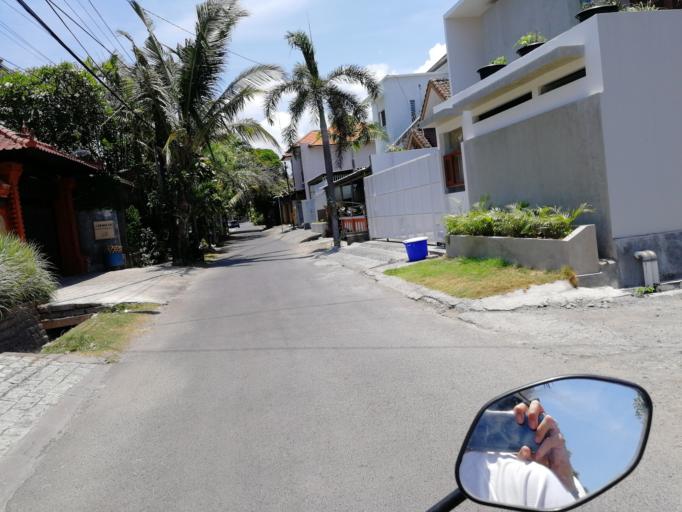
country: ID
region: Bali
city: Dajan Tangluk
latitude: -8.6652
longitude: 115.2356
